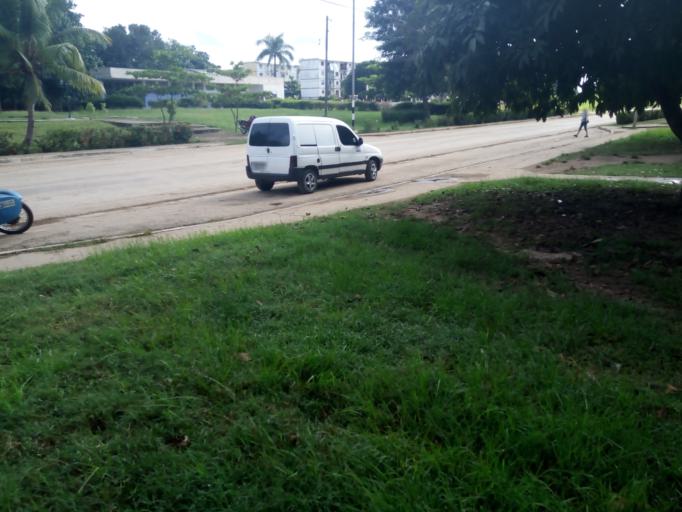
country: CU
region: Sancti Spiritus
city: La Sierpe
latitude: 21.7726
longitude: -79.2698
